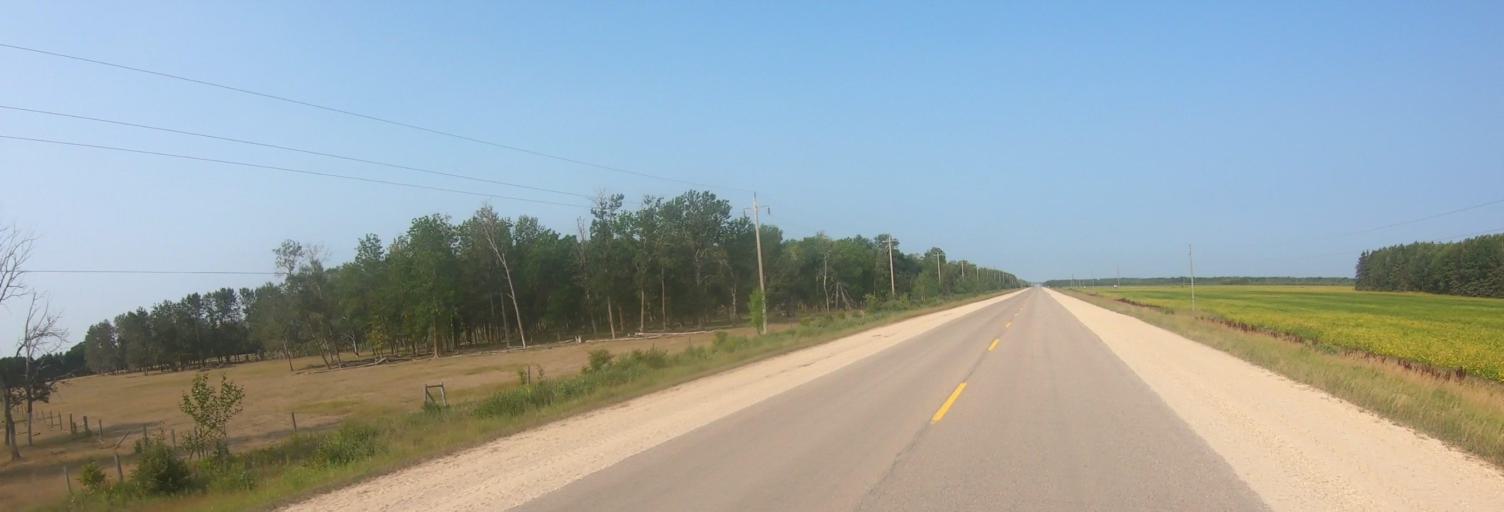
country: US
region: Minnesota
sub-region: Roseau County
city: Roseau
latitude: 49.0233
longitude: -95.5913
